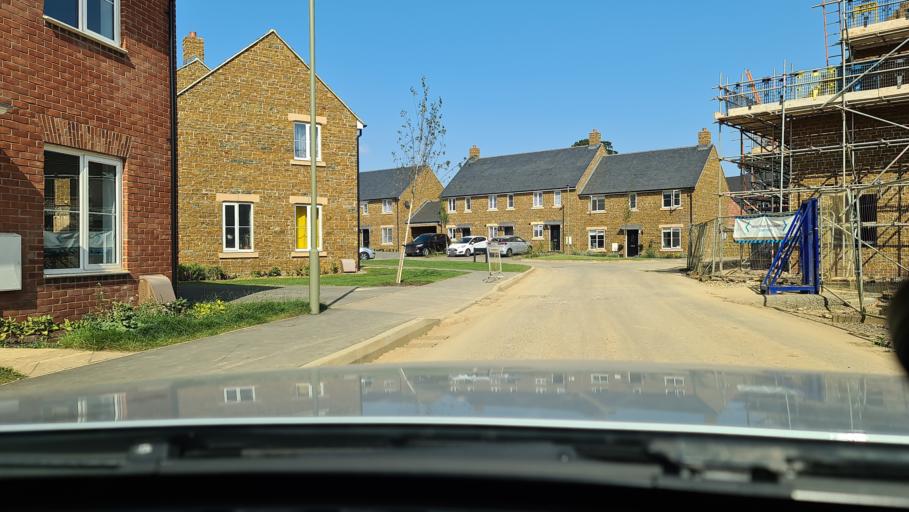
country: GB
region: England
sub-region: Oxfordshire
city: Hanwell
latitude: 52.0774
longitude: -1.3686
